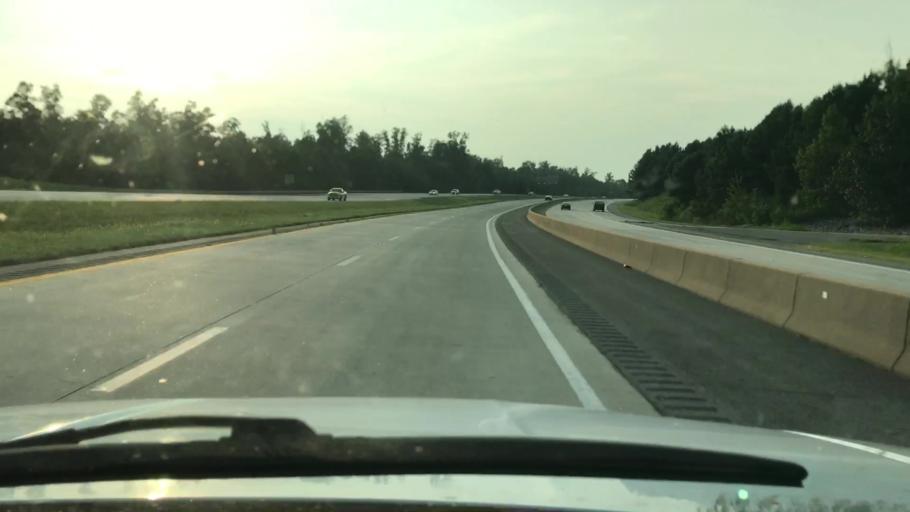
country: US
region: Virginia
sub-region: Chesterfield County
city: Brandermill
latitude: 37.4697
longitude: -77.6493
